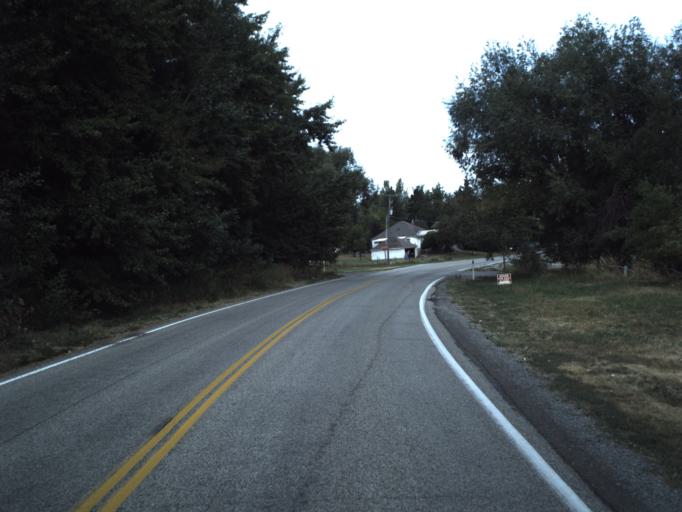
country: US
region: Utah
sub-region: Cache County
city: Mendon
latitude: 41.7032
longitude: -111.9789
